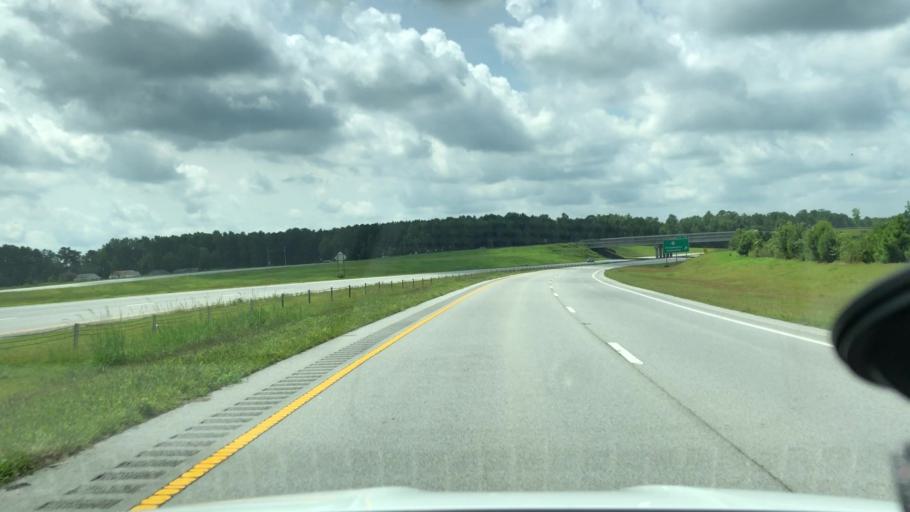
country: US
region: North Carolina
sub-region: Beaufort County
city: Washington
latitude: 35.5098
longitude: -77.0875
